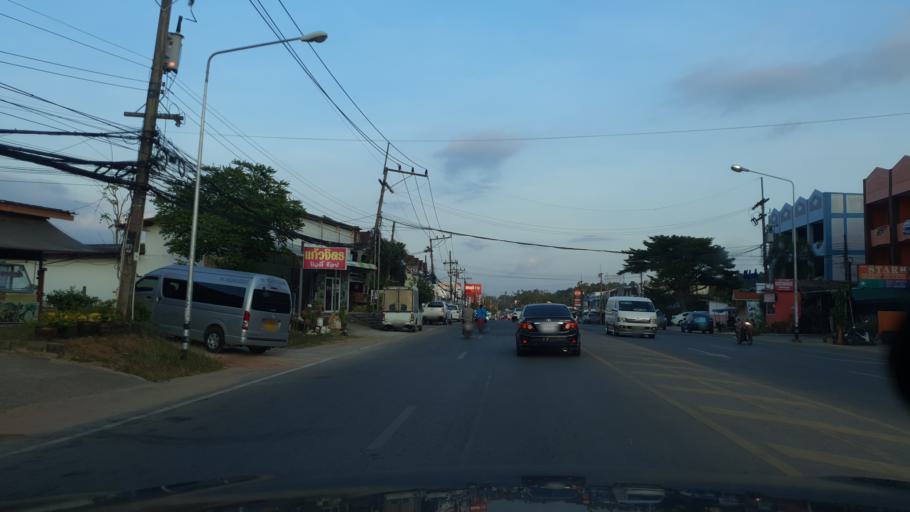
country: TH
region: Phangnga
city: Ban Ao Nang
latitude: 8.0416
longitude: 98.8378
